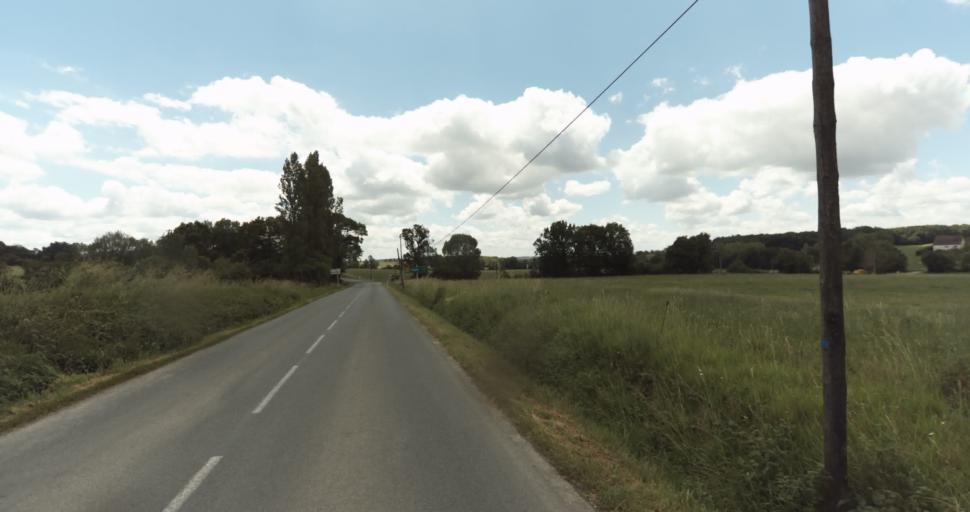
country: FR
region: Aquitaine
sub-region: Departement du Lot-et-Garonne
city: Villereal
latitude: 44.6891
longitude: 0.7533
